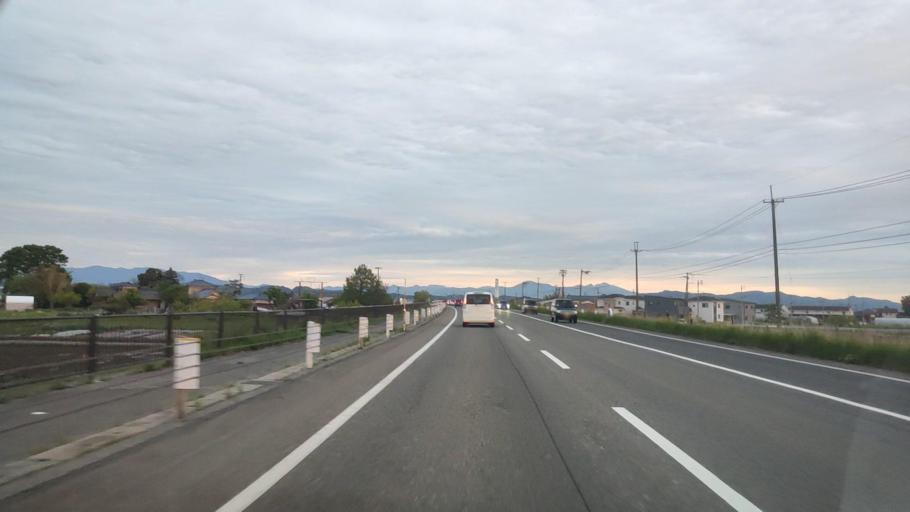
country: JP
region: Niigata
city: Niitsu-honcho
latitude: 37.8009
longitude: 139.1038
